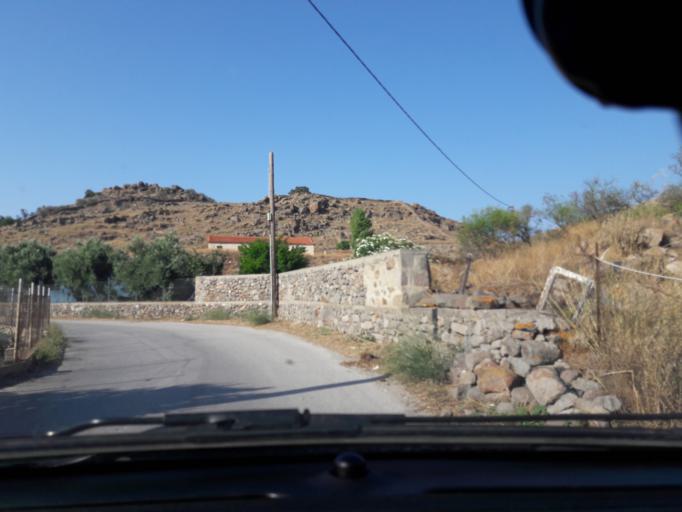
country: GR
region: North Aegean
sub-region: Nomos Lesvou
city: Myrina
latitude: 39.8466
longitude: 25.0850
